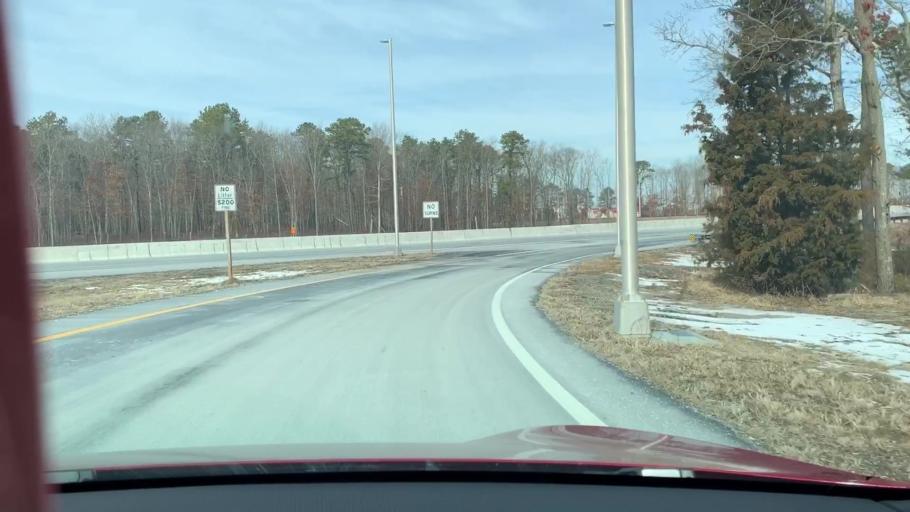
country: US
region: New Jersey
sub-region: Atlantic County
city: Northfield
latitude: 39.3956
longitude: -74.5623
